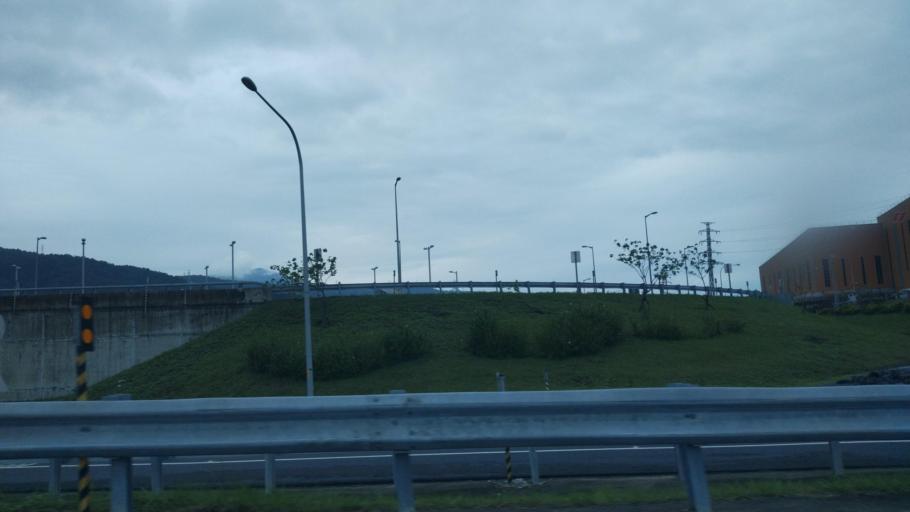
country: TW
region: Taiwan
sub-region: Yilan
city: Yilan
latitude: 24.6221
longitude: 121.8176
